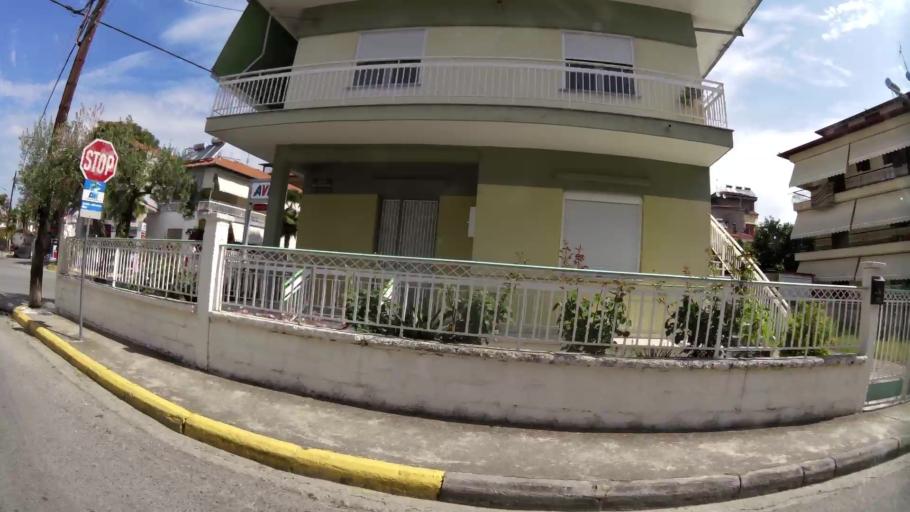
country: GR
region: Central Macedonia
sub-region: Nomos Pierias
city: Katerini
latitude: 40.2677
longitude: 22.4978
